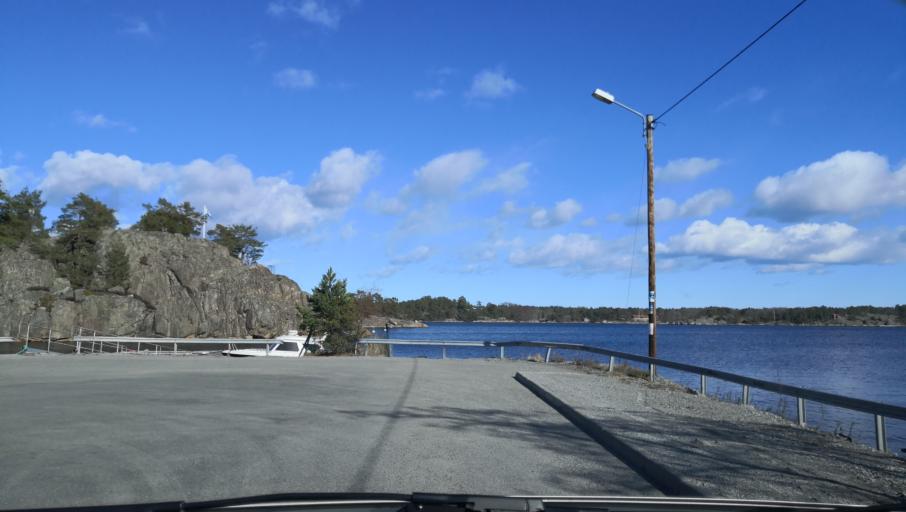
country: SE
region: Stockholm
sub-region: Varmdo Kommun
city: Holo
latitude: 59.3569
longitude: 18.6349
